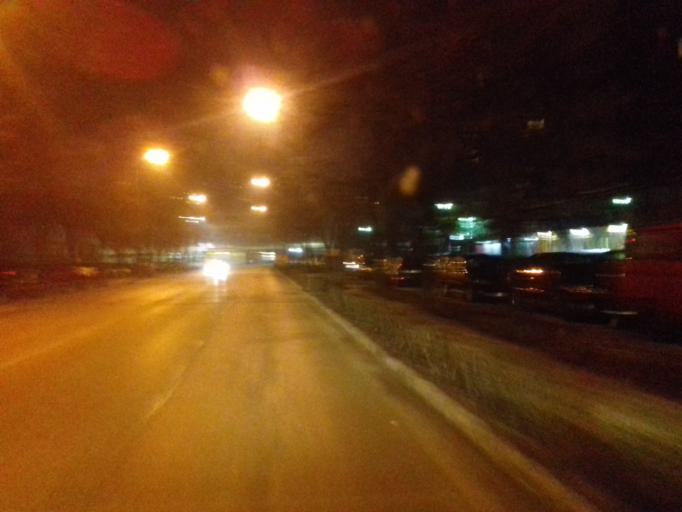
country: BA
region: Federation of Bosnia and Herzegovina
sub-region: Kanton Sarajevo
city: Sarajevo
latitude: 43.8488
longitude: 18.3865
